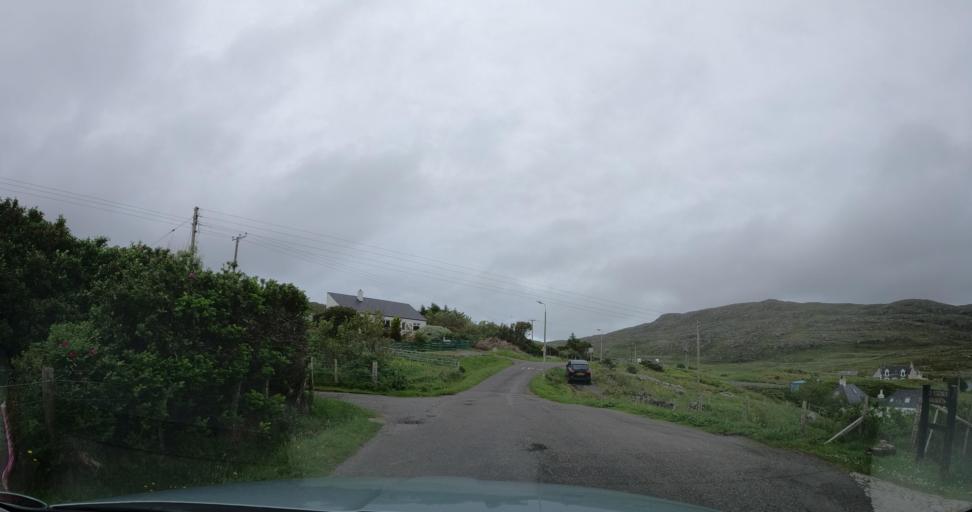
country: GB
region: Scotland
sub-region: Eilean Siar
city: Barra
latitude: 56.9576
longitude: -7.5058
